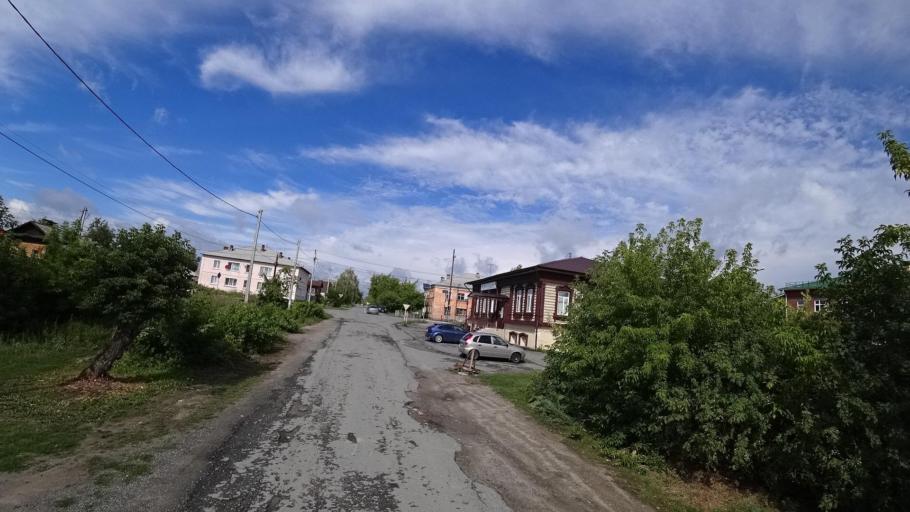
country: RU
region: Sverdlovsk
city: Kamyshlov
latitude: 56.8385
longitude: 62.7101
